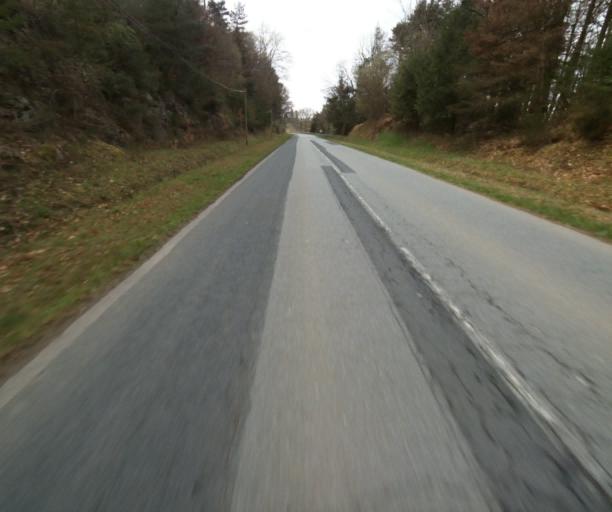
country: FR
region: Limousin
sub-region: Departement de la Correze
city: Correze
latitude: 45.3889
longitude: 1.8643
